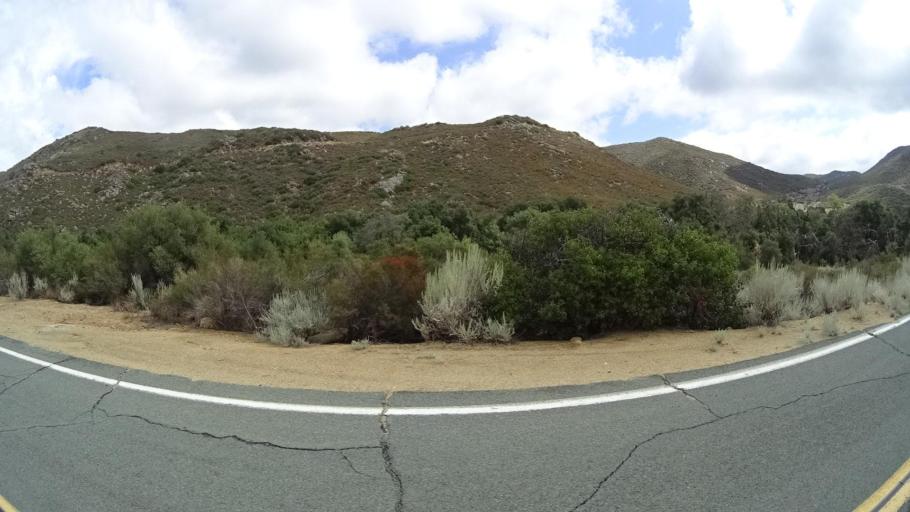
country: US
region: California
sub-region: San Diego County
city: Pine Valley
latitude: 32.7815
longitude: -116.4498
